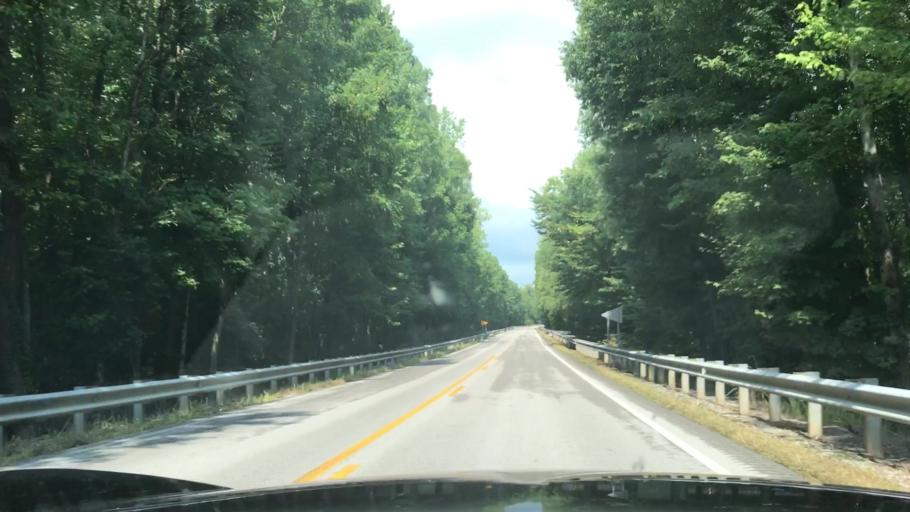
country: US
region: Kentucky
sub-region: Ohio County
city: Oak Grove
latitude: 37.2074
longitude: -86.8931
